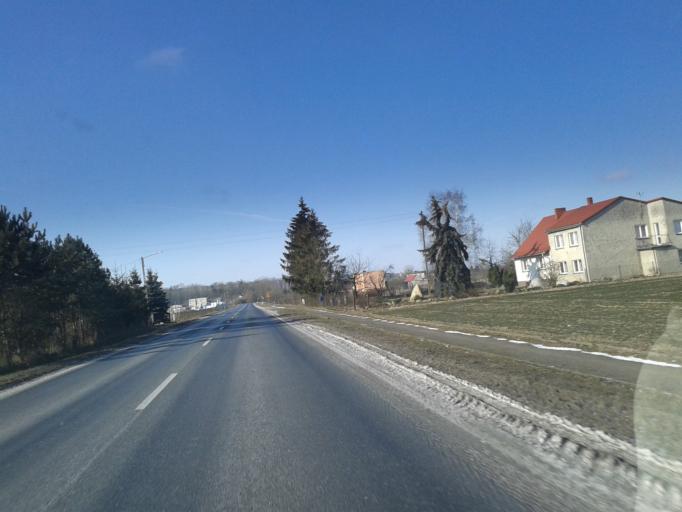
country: PL
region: Greater Poland Voivodeship
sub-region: Powiat pilski
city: Wysoka
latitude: 53.1378
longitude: 17.0705
